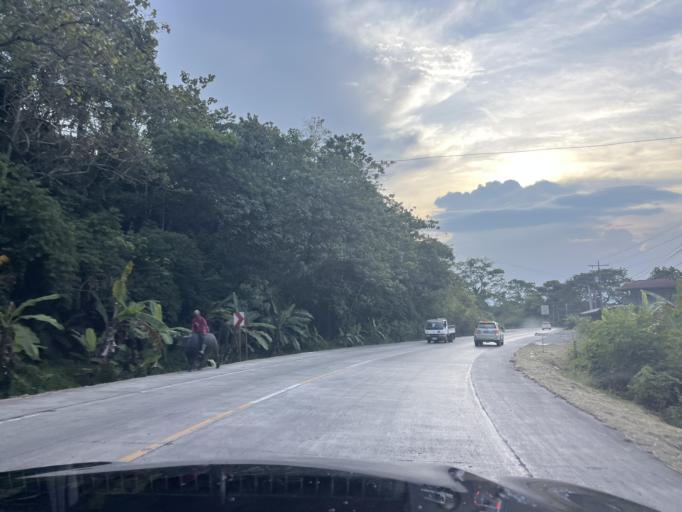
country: PH
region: Northern Mindanao
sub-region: Province of Bukidnon
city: Dalorong
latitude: 7.6047
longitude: 125.1530
